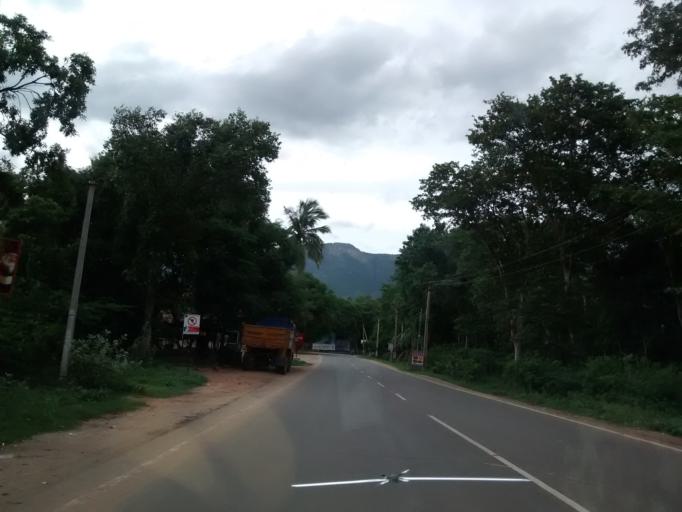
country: IN
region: Andhra Pradesh
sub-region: Chittoor
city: Narasingapuram
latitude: 13.6149
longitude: 79.3633
